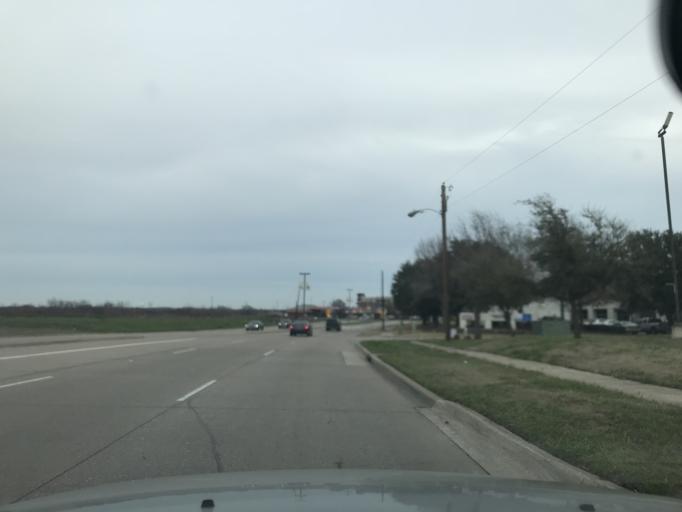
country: US
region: Texas
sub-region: Dallas County
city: Carrollton
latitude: 32.9932
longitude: -96.9413
